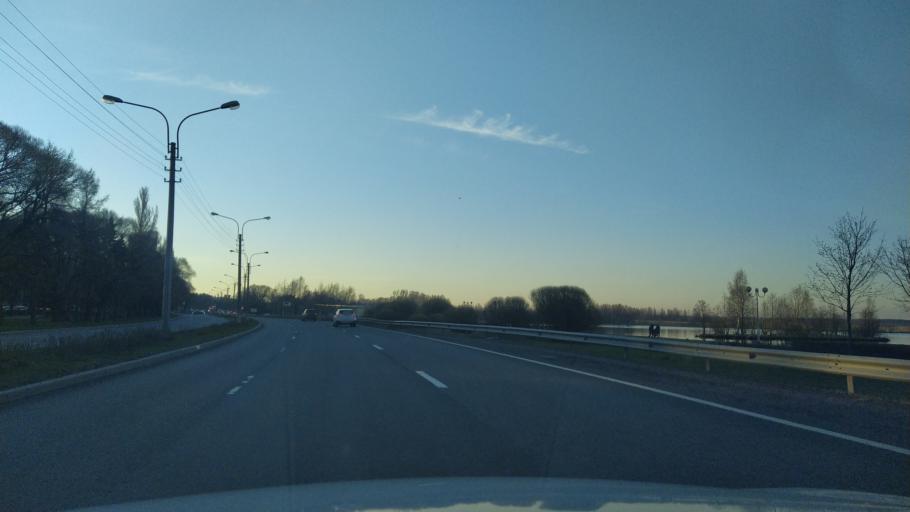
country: RU
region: St.-Petersburg
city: Sestroretsk
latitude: 60.1012
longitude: 29.9798
